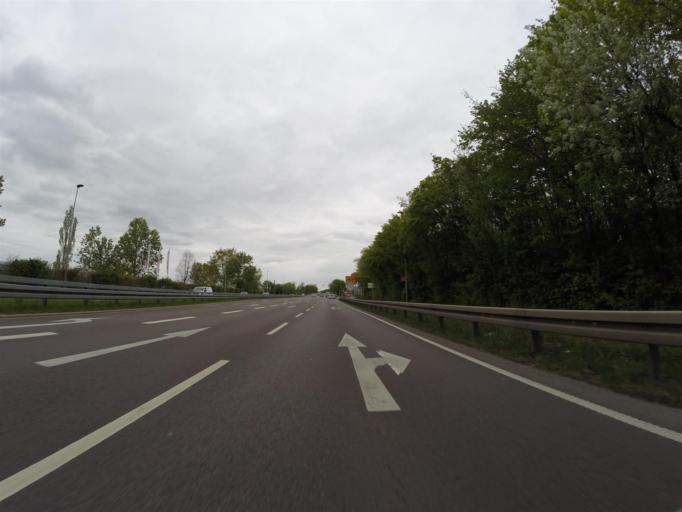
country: DE
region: Saxony-Anhalt
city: Merseburg
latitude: 51.3709
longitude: 11.9803
